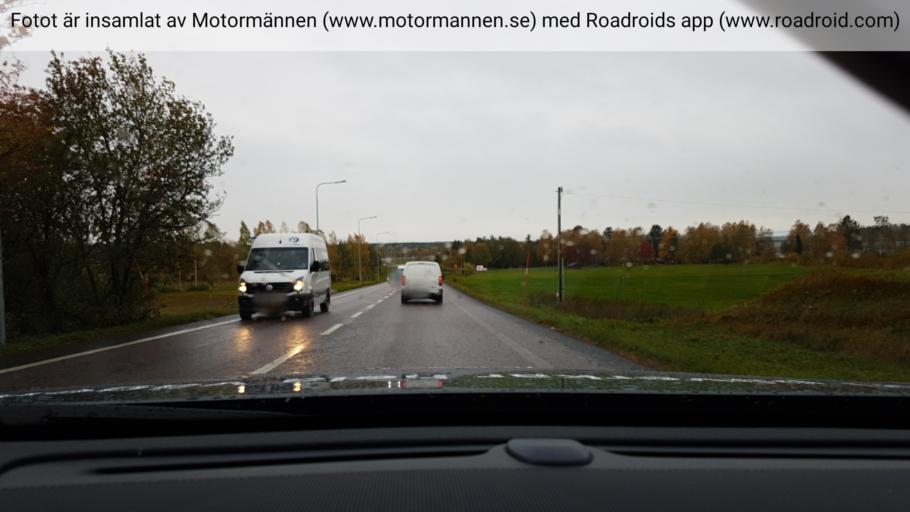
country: SE
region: Norrbotten
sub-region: Lulea Kommun
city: Bergnaset
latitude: 65.5807
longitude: 22.0622
